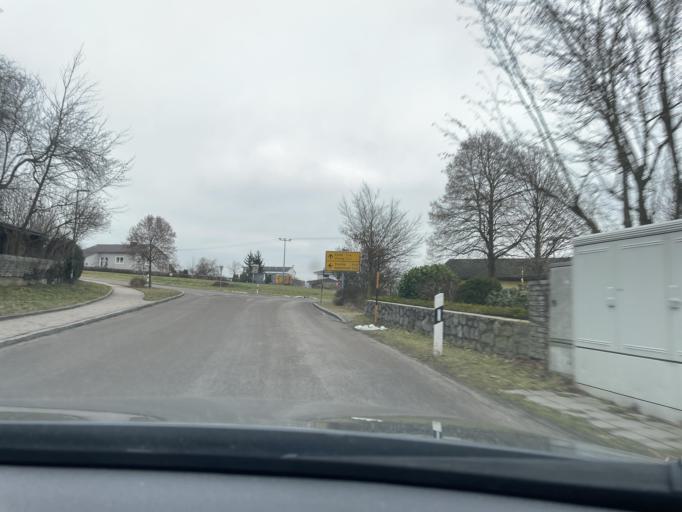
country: DE
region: Bavaria
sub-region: Upper Palatinate
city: Cham
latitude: 49.1942
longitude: 12.6856
